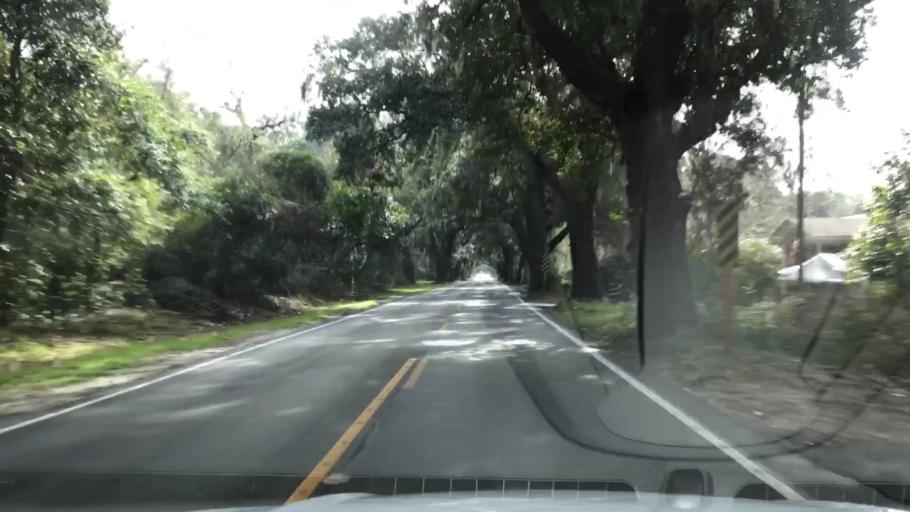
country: US
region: South Carolina
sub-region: Charleston County
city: Shell Point
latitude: 32.7389
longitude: -80.0347
